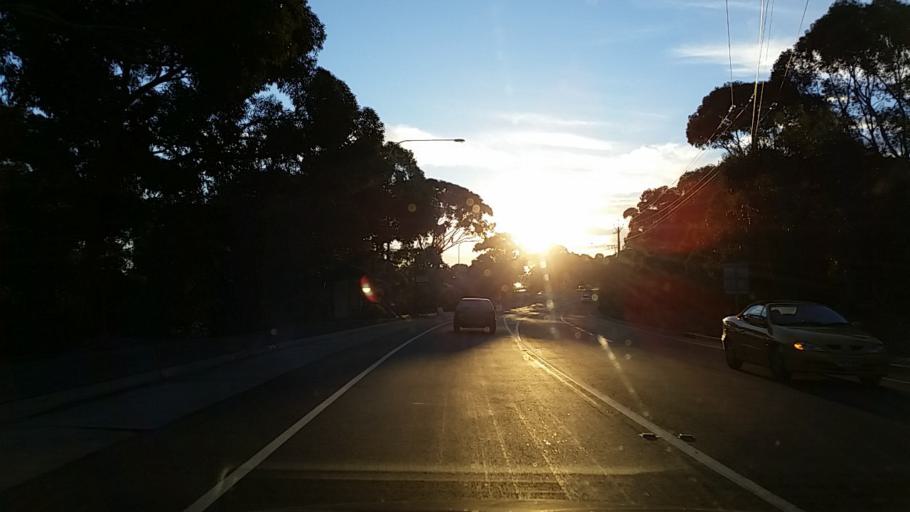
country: AU
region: South Australia
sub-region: Onkaparinga
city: Craigburn Farm
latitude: -35.0586
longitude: 138.6031
